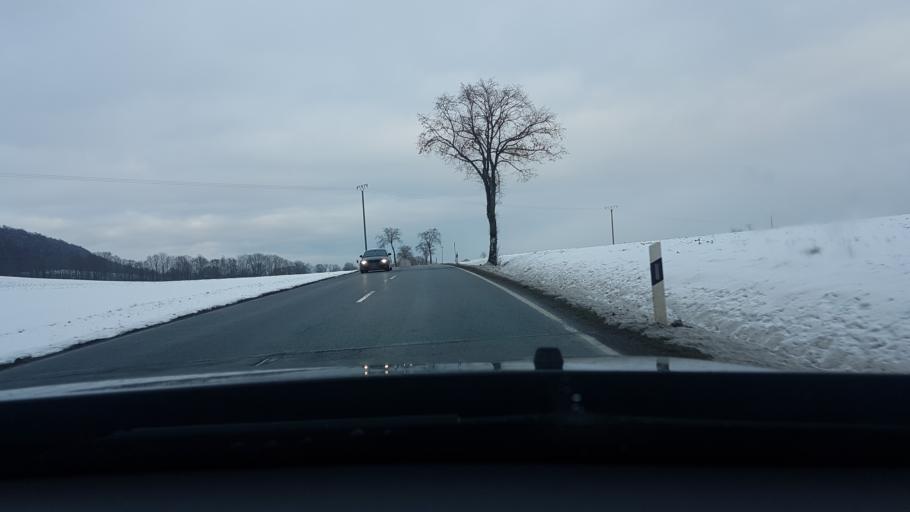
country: DE
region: Hesse
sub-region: Regierungsbezirk Kassel
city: Korbach
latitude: 51.2885
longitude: 8.8071
